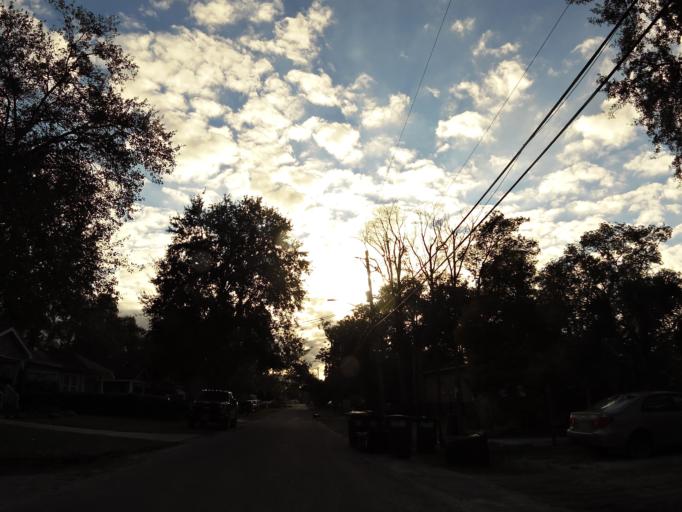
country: US
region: Florida
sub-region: Duval County
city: Jacksonville
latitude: 30.3107
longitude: -81.7114
